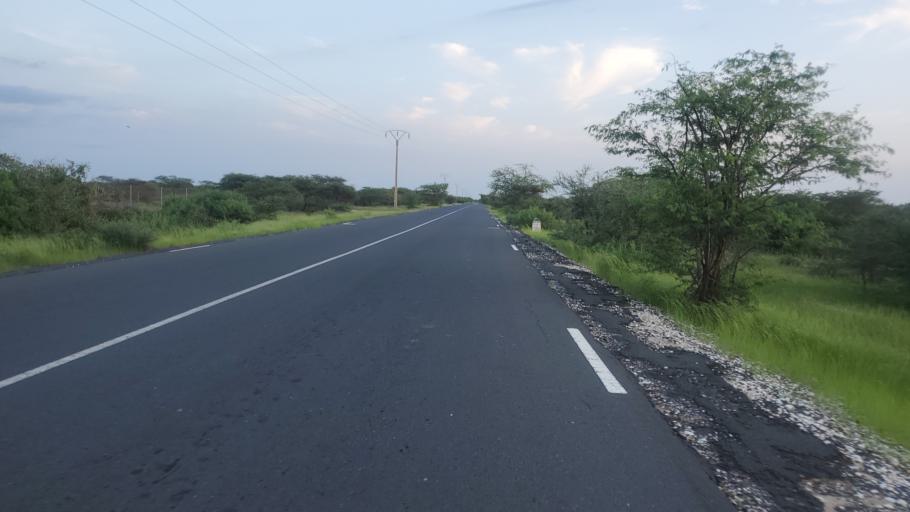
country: SN
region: Saint-Louis
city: Saint-Louis
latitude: 16.1179
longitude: -16.4141
